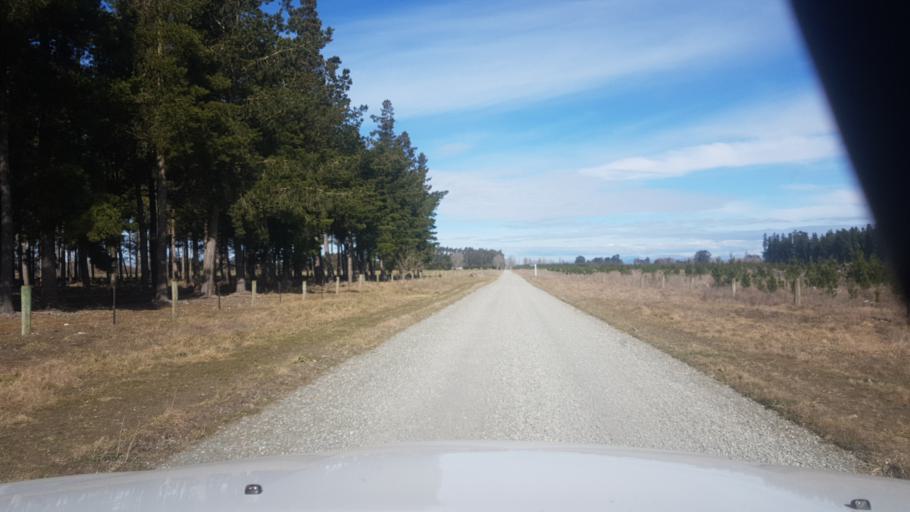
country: NZ
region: Canterbury
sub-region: Timaru District
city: Pleasant Point
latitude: -44.1305
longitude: 171.2799
